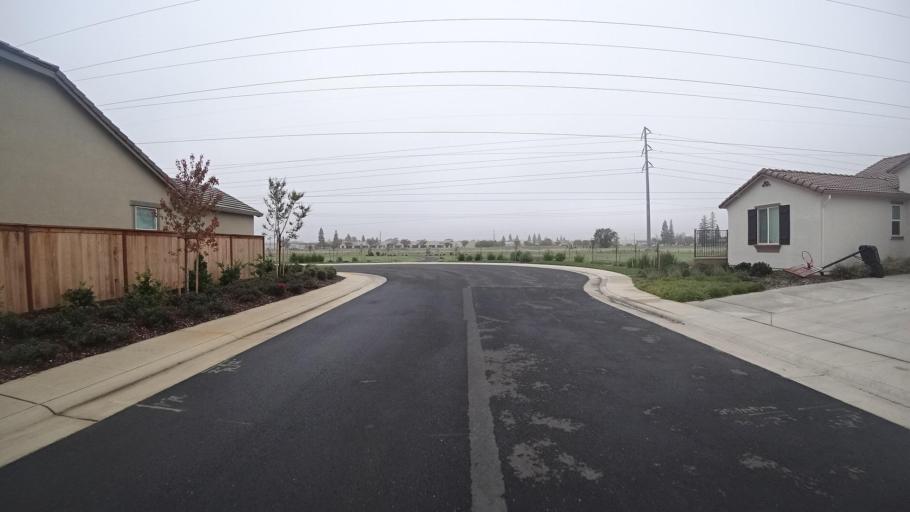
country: US
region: California
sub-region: Sacramento County
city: Elk Grove
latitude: 38.3992
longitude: -121.3497
